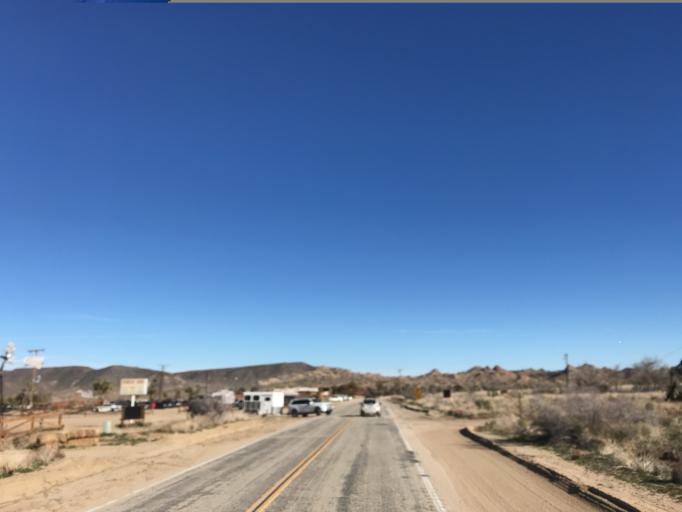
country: US
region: California
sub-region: San Bernardino County
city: Yucca Valley
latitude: 34.1561
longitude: -116.4955
